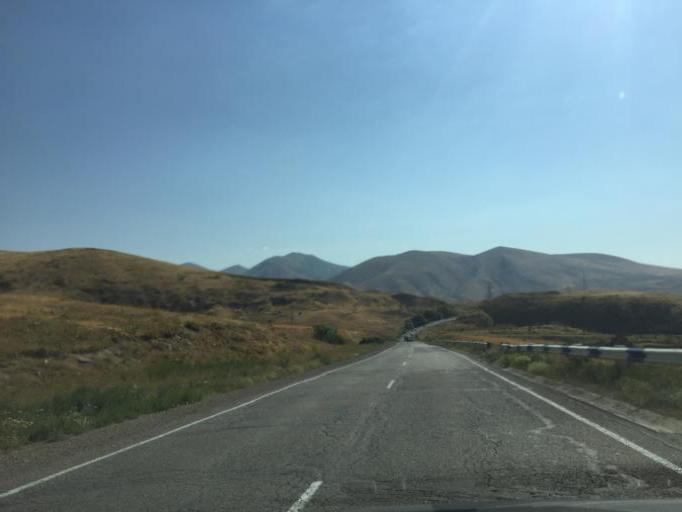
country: AM
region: Ararat
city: Zangakatun
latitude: 39.8190
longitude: 45.0083
